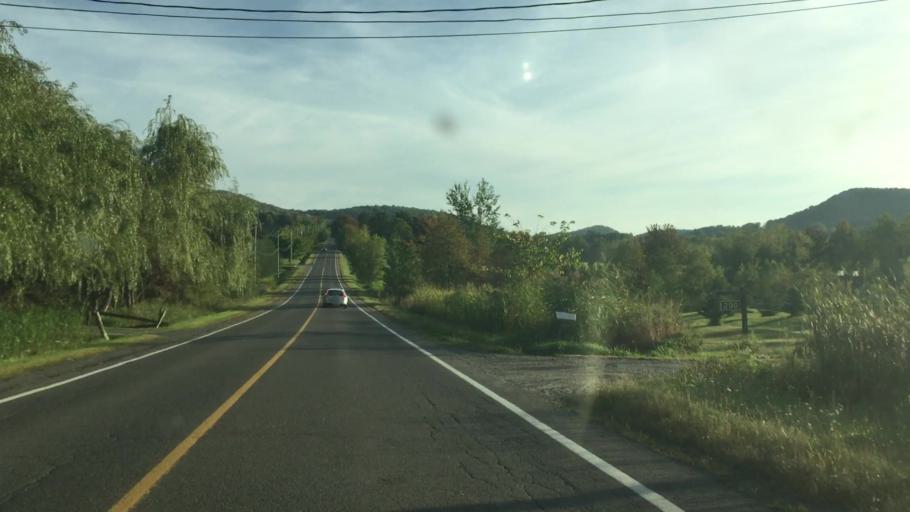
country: CA
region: Quebec
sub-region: Monteregie
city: Bromont
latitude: 45.3060
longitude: -72.6588
